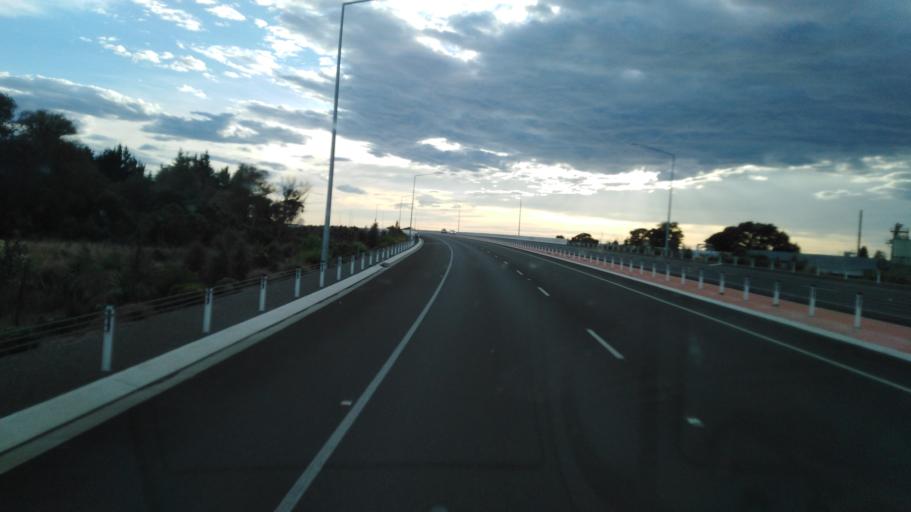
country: NZ
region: Canterbury
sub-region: Waimakariri District
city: Kaiapoi
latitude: -43.4370
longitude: 172.6317
